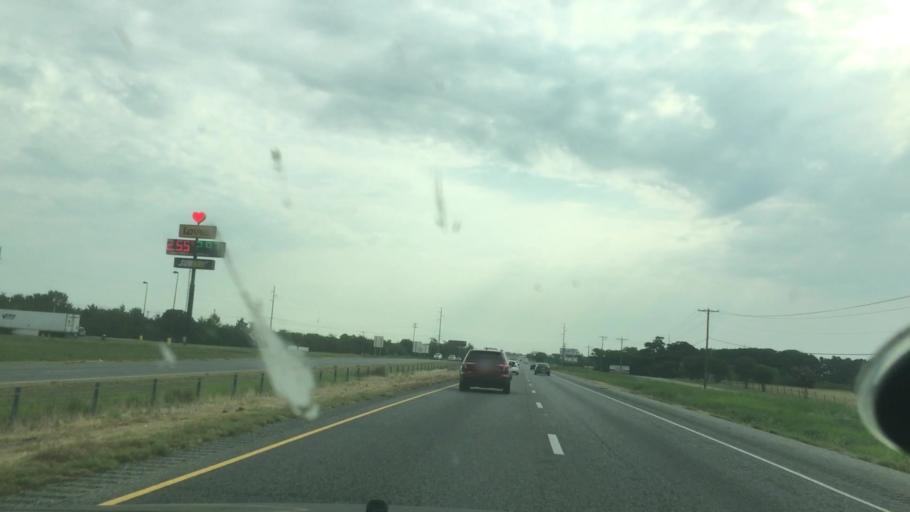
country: US
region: Oklahoma
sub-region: Bryan County
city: Colbert
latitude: 33.8791
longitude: -96.4986
